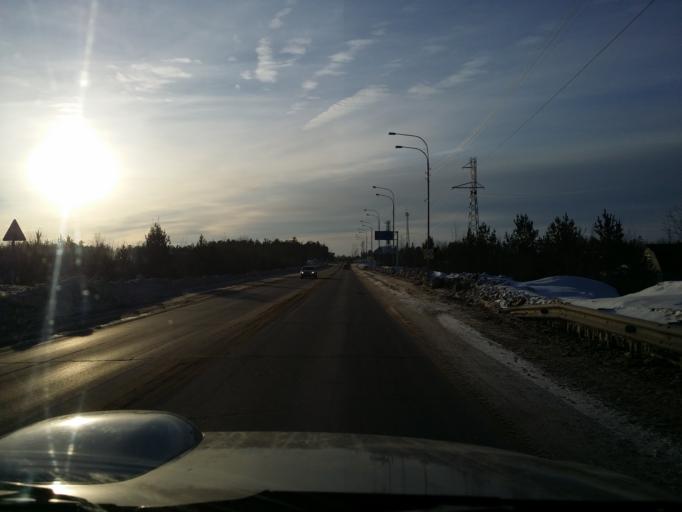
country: RU
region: Khanty-Mansiyskiy Avtonomnyy Okrug
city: Izluchinsk
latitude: 60.9649
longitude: 76.8561
